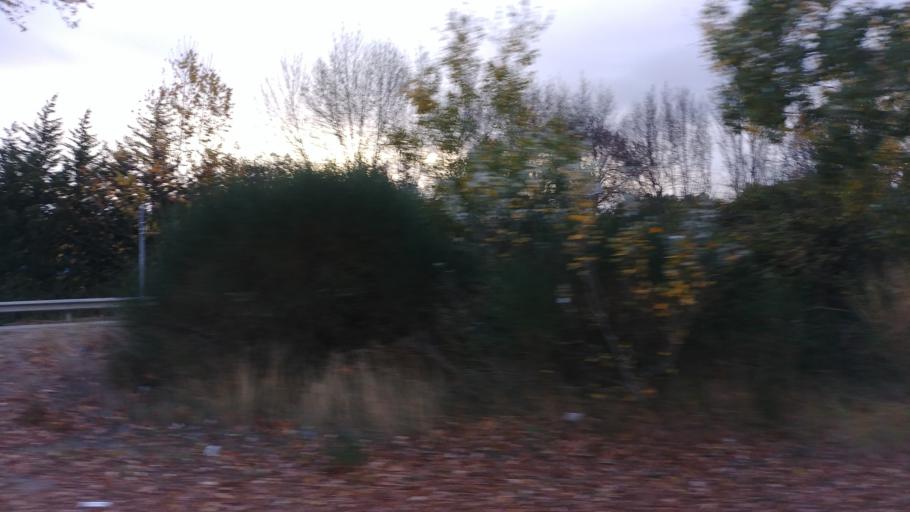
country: FR
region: Provence-Alpes-Cote d'Azur
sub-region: Departement des Bouches-du-Rhone
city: Venelles
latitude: 43.5749
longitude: 5.4685
